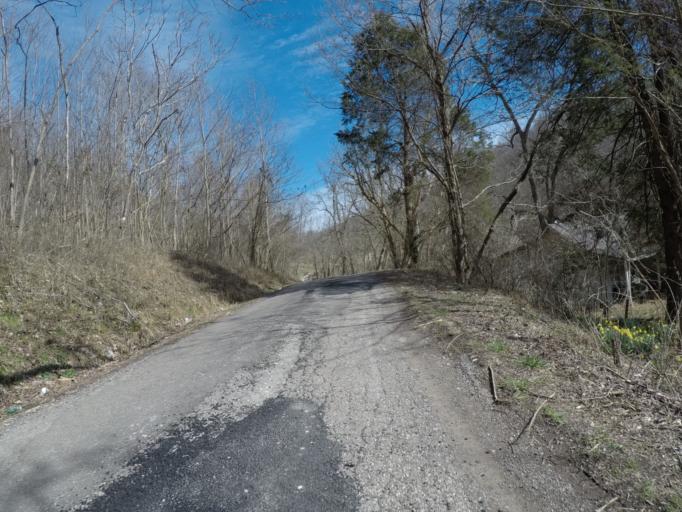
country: US
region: West Virginia
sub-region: Wayne County
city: Ceredo
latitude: 38.3483
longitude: -82.5578
